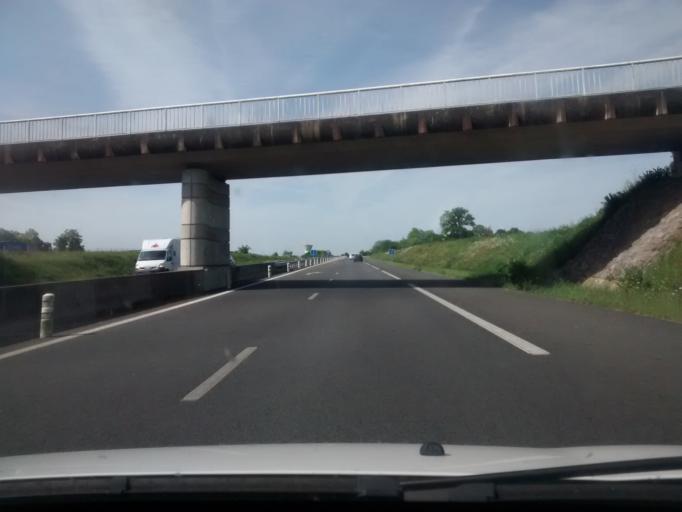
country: FR
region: Brittany
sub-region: Departement d'Ille-et-Vilaine
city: Romagne
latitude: 48.3482
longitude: -1.2838
